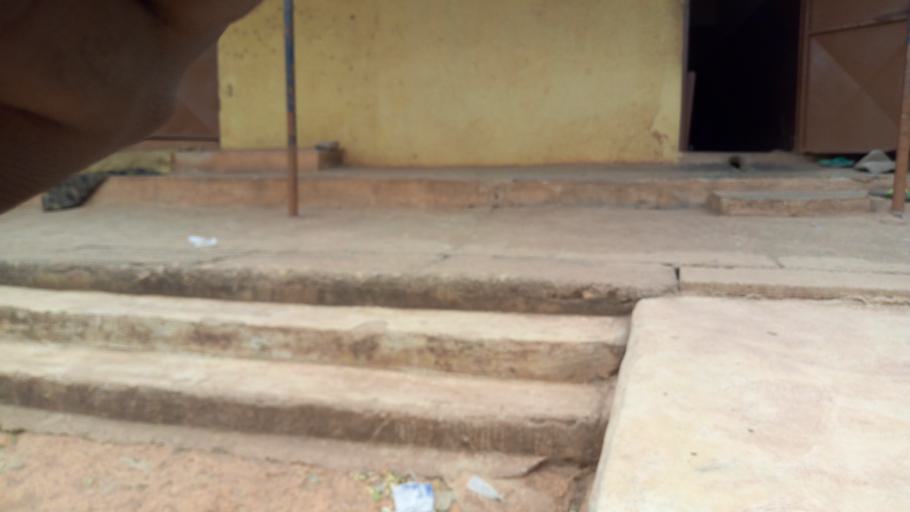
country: CI
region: Vallee du Bandama
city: Bouake
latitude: 7.7134
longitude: -5.0276
